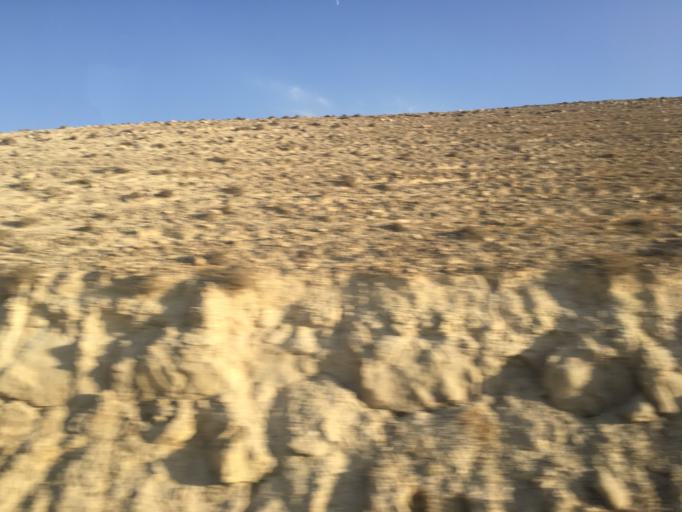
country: IL
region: Southern District
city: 'Arad
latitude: 31.3036
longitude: 35.2529
